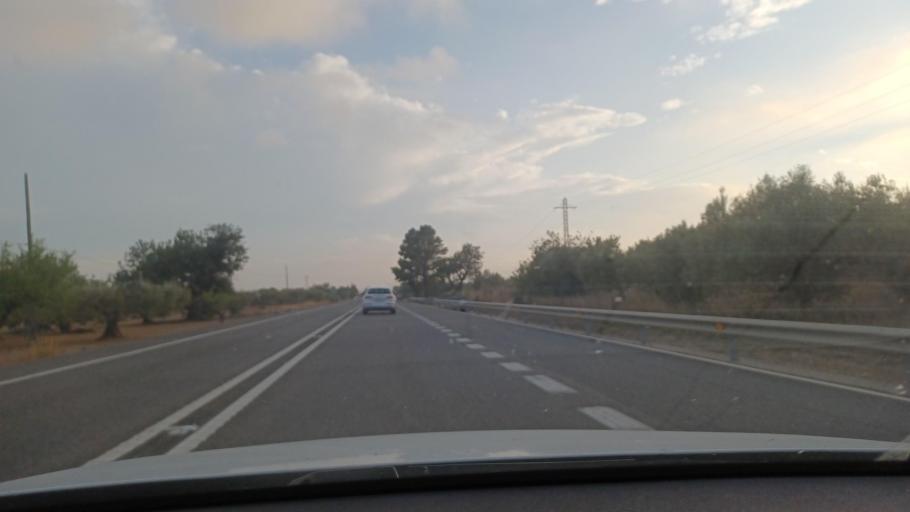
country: ES
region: Catalonia
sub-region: Provincia de Tarragona
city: L'Ampolla
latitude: 40.8343
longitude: 0.7101
